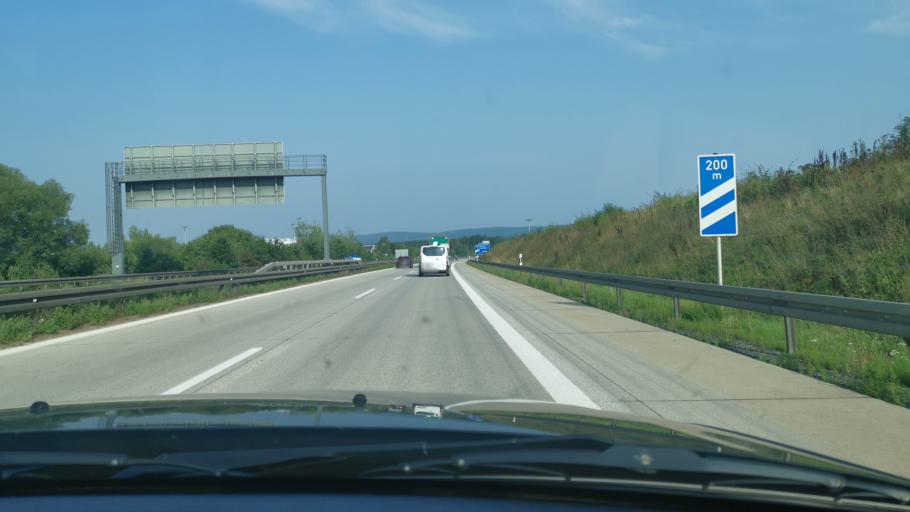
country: DE
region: Bavaria
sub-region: Upper Palatinate
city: Wernberg-Koblitz
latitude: 49.5288
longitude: 12.1468
